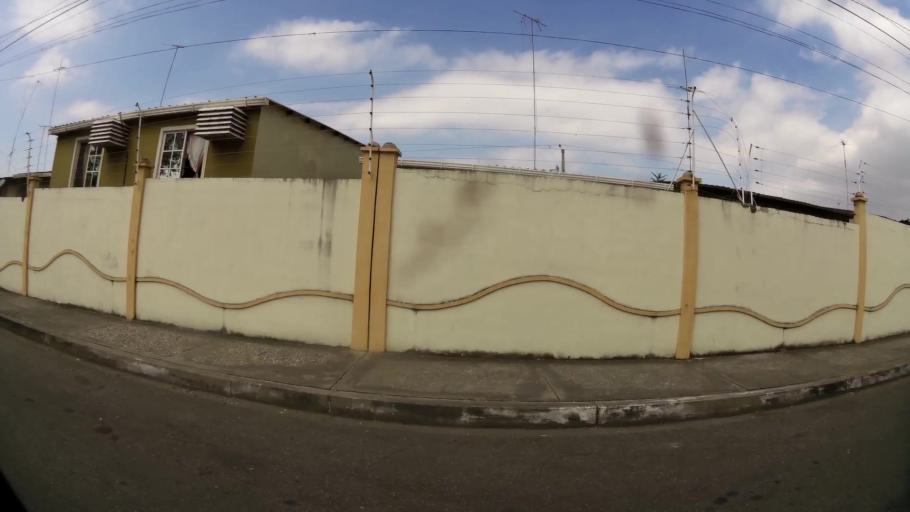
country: EC
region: Guayas
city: Santa Lucia
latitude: -2.0873
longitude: -79.9408
